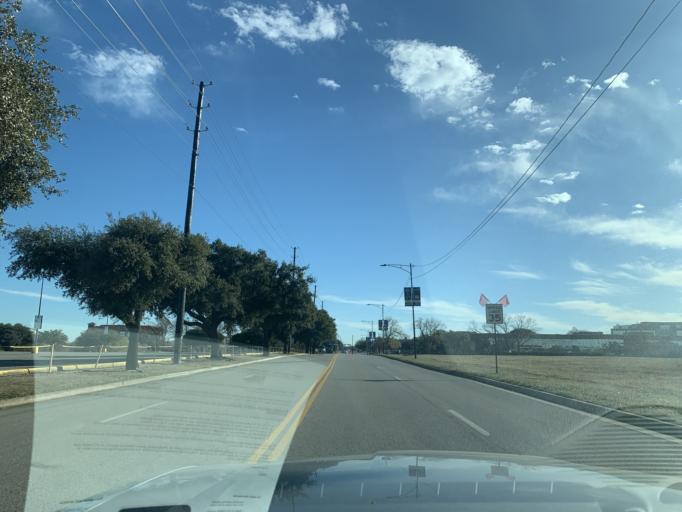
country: US
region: Texas
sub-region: Tarrant County
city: Arlington
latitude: 32.7525
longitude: -97.0721
